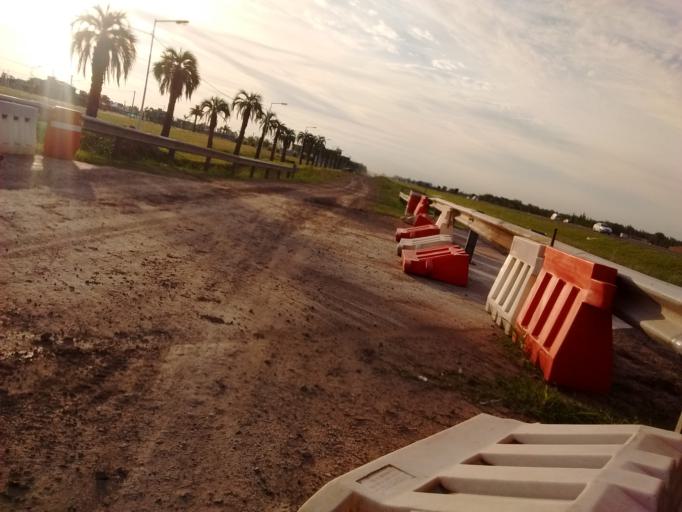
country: AR
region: Santa Fe
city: Roldan
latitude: -32.9309
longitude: -60.8726
